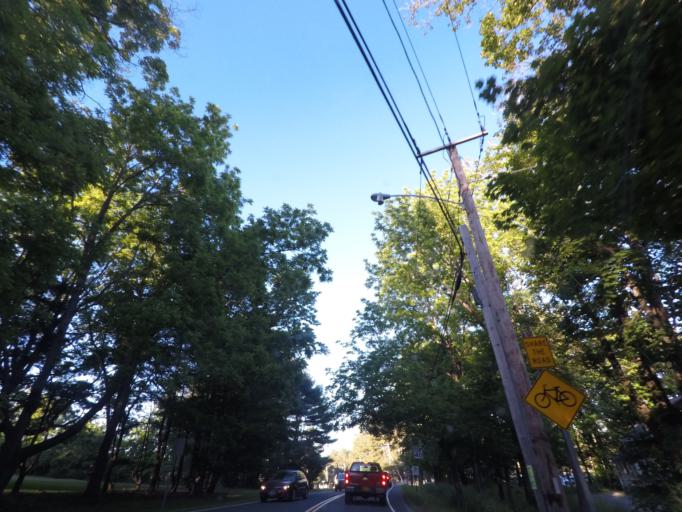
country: US
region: Massachusetts
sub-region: Berkshire County
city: Lenox
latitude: 42.3521
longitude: -73.3143
